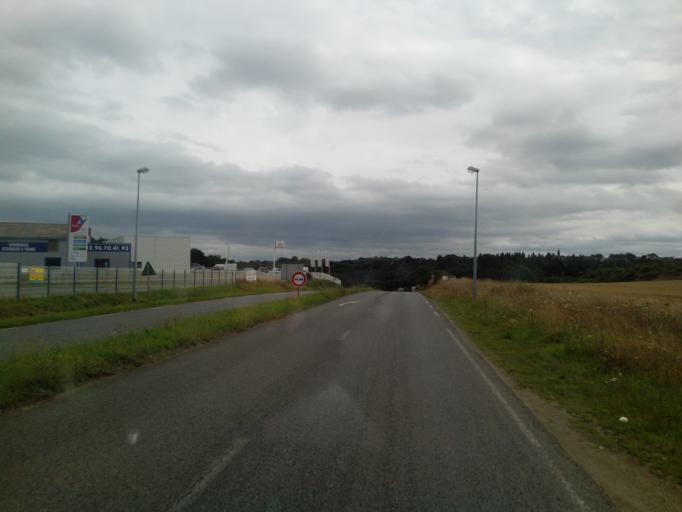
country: FR
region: Brittany
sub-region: Departement des Cotes-d'Armor
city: Etables-sur-Mer
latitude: 48.6421
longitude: -2.8366
